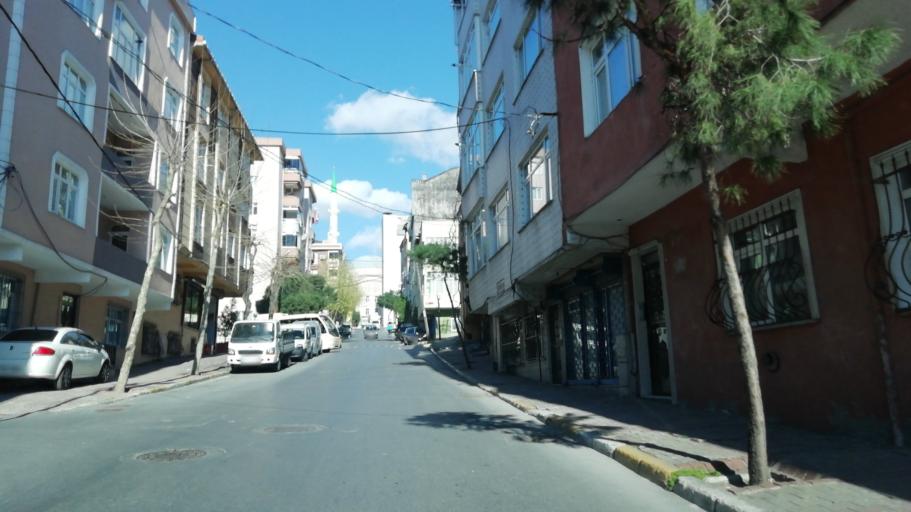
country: TR
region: Istanbul
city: Bagcilar
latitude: 41.0496
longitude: 28.8560
